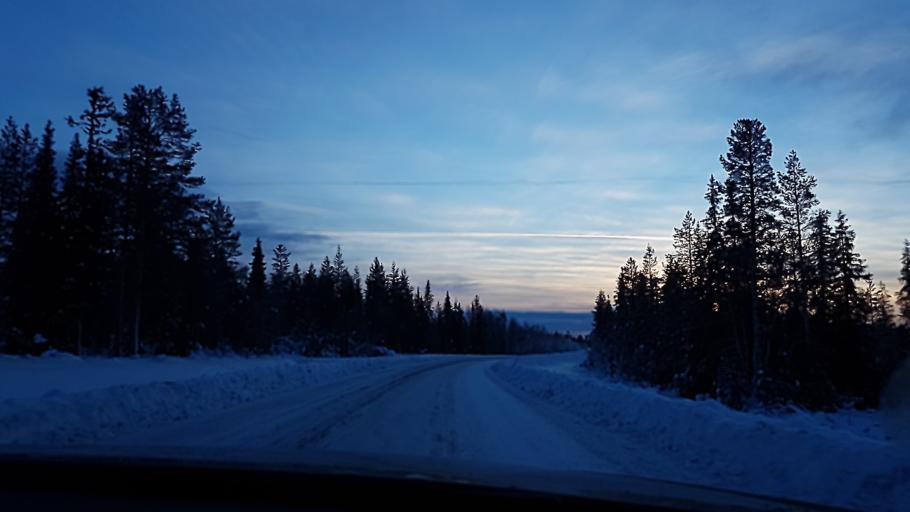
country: SE
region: Norrbotten
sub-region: Jokkmokks Kommun
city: Jokkmokk
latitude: 66.1074
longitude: 20.0543
